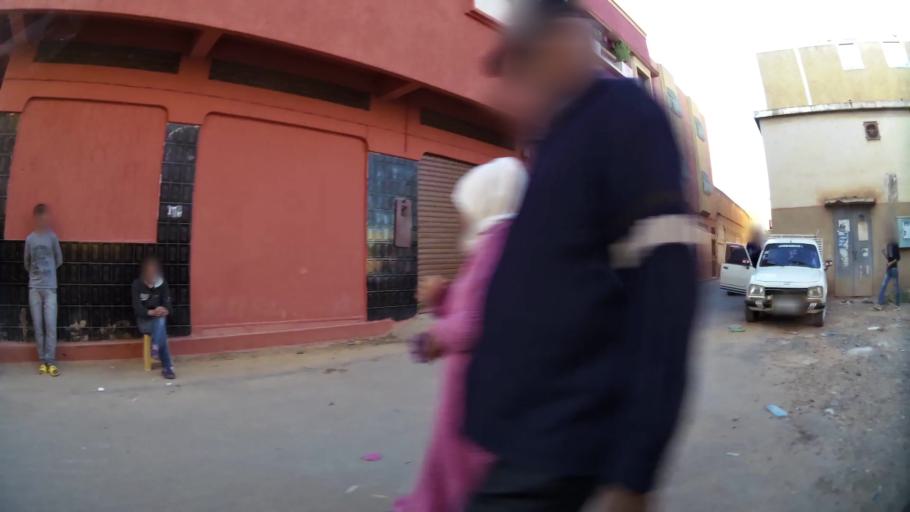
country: MA
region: Oriental
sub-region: Berkane-Taourirt
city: Berkane
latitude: 34.9217
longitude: -2.3146
